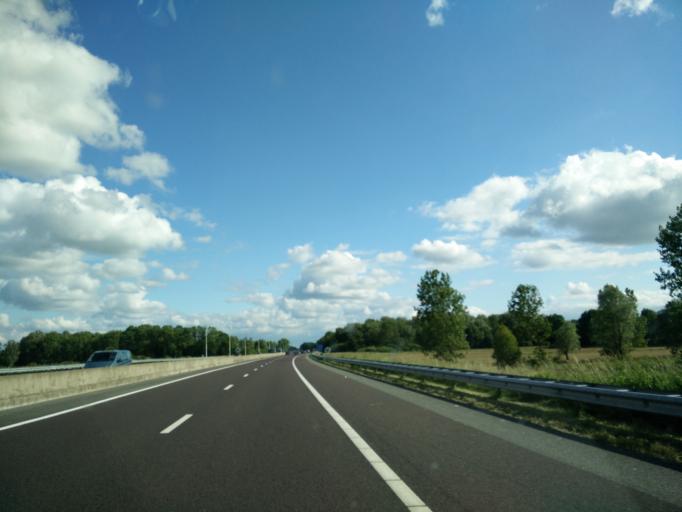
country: NL
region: Groningen
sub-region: Gemeente Haren
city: Haren
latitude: 53.1428
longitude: 6.6076
